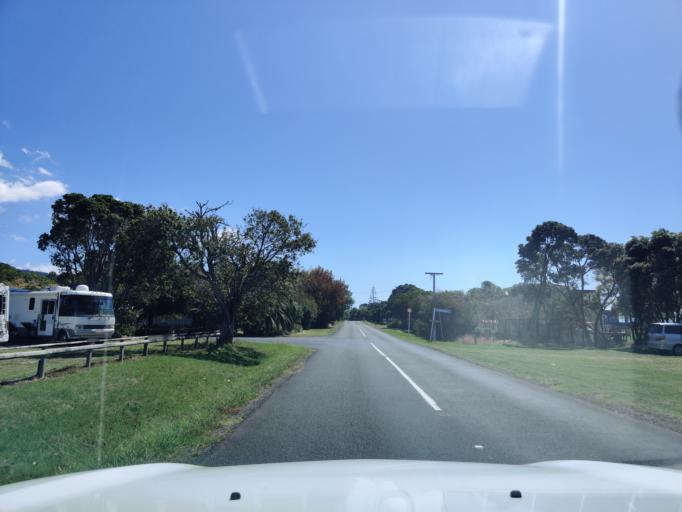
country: NZ
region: Waikato
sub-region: Thames-Coromandel District
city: Thames
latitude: -37.0495
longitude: 175.3000
